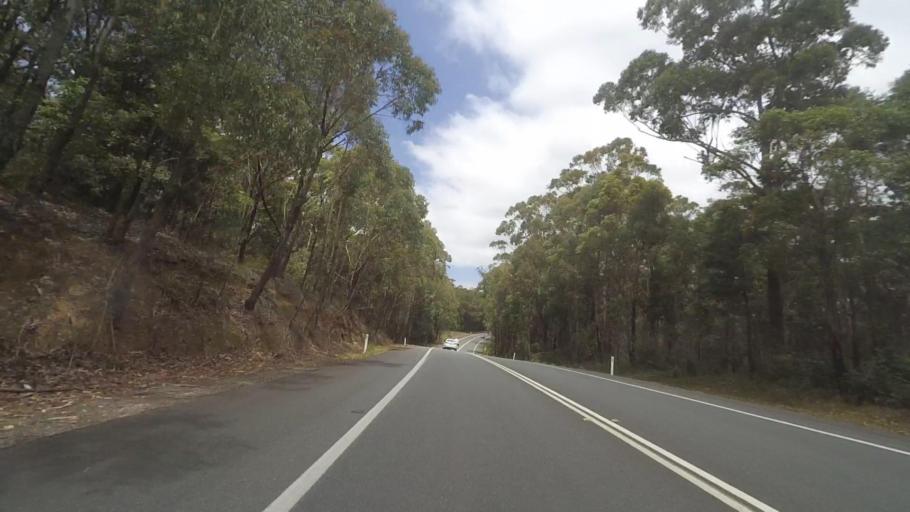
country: AU
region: New South Wales
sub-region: Shoalhaven Shire
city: Milton
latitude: -35.1549
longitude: 150.4507
